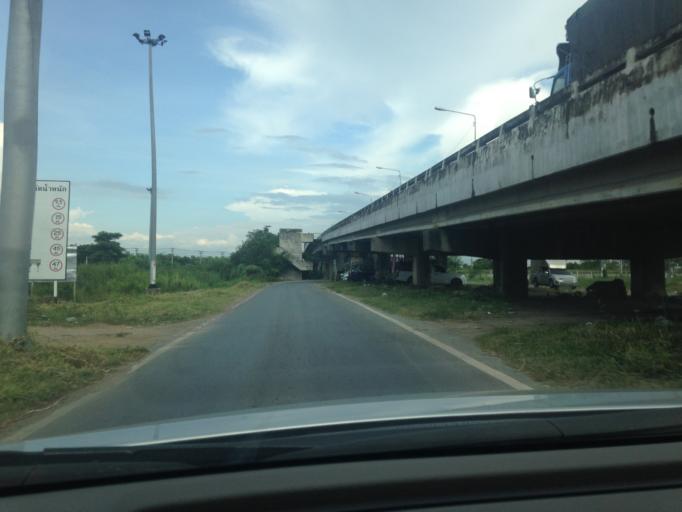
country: TH
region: Pathum Thani
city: Khlong Luang
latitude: 14.0671
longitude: 100.6950
